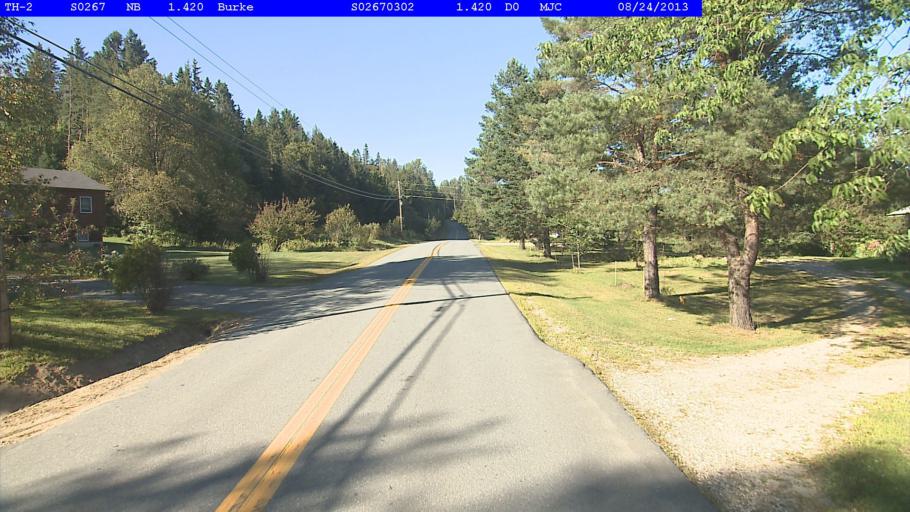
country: US
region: Vermont
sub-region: Caledonia County
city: Lyndonville
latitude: 44.6066
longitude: -71.9376
